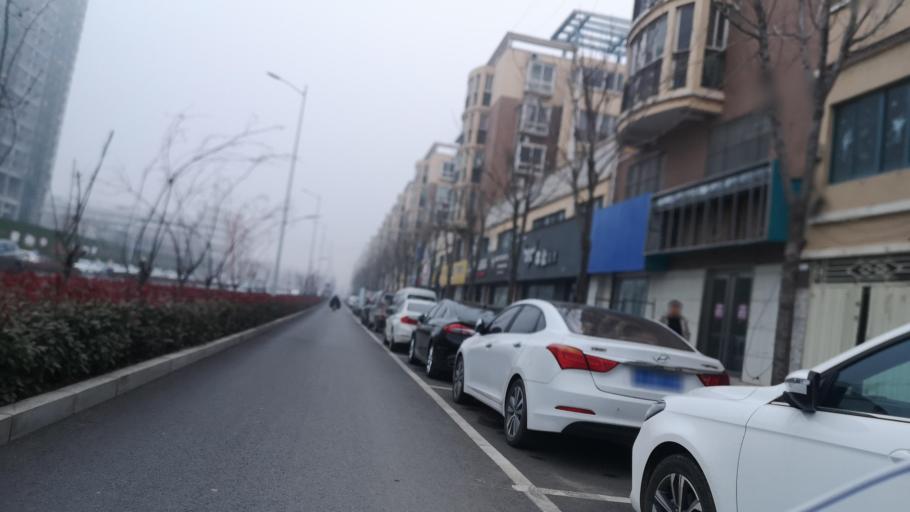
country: CN
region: Henan Sheng
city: Zhongyuanlu
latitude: 35.7644
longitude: 115.0846
